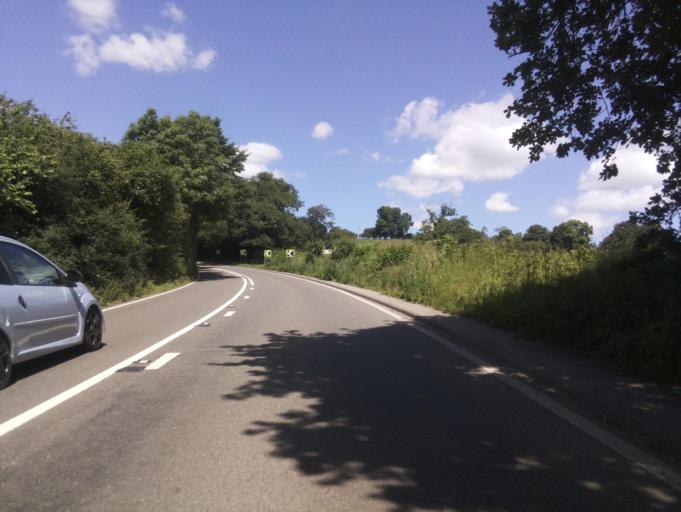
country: GB
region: England
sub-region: Derbyshire
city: Ashbourne
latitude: 53.0369
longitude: -1.7340
